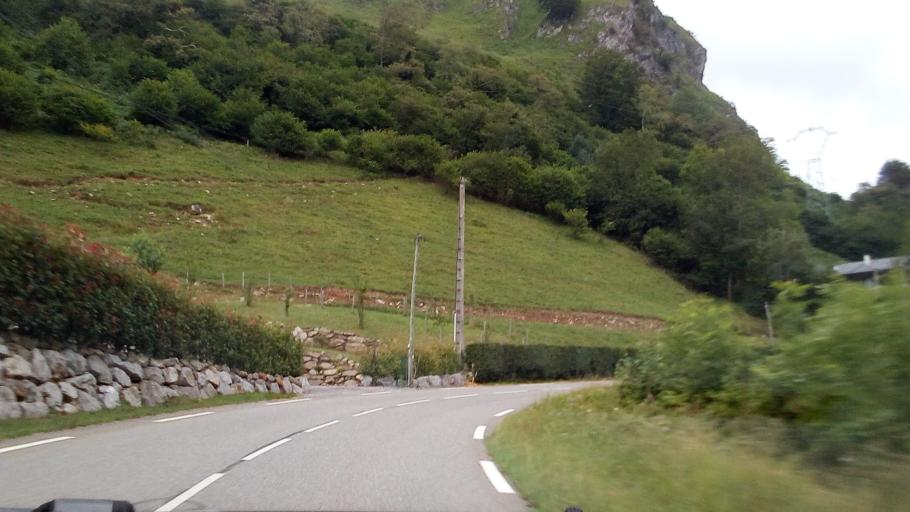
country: FR
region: Aquitaine
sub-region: Departement des Pyrenees-Atlantiques
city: Laruns
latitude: 42.9689
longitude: -0.3711
